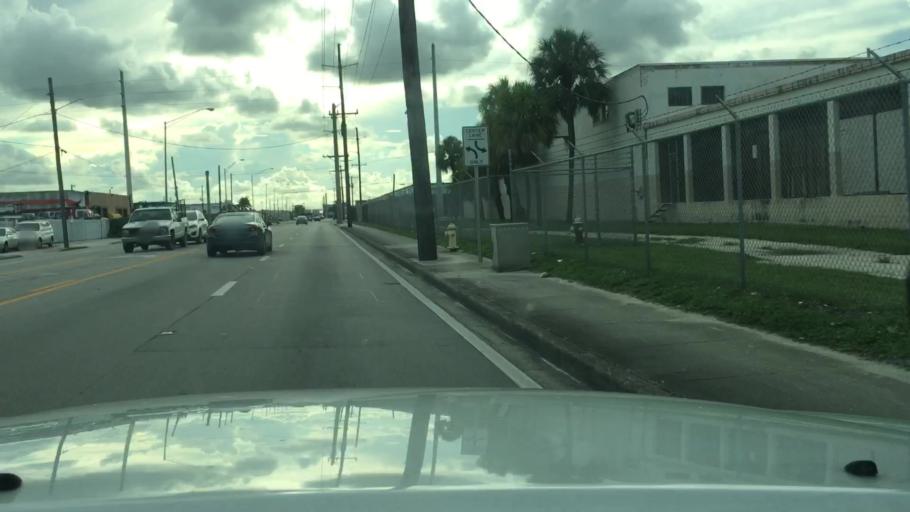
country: US
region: Florida
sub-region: Miami-Dade County
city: Brownsville
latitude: 25.8237
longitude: -80.2514
